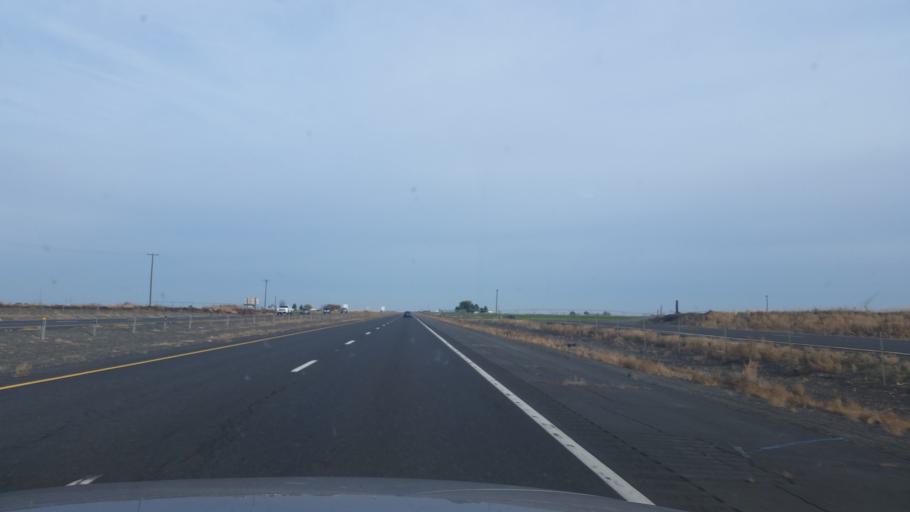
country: US
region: Washington
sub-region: Grant County
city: Quincy
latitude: 47.1033
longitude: -119.8154
